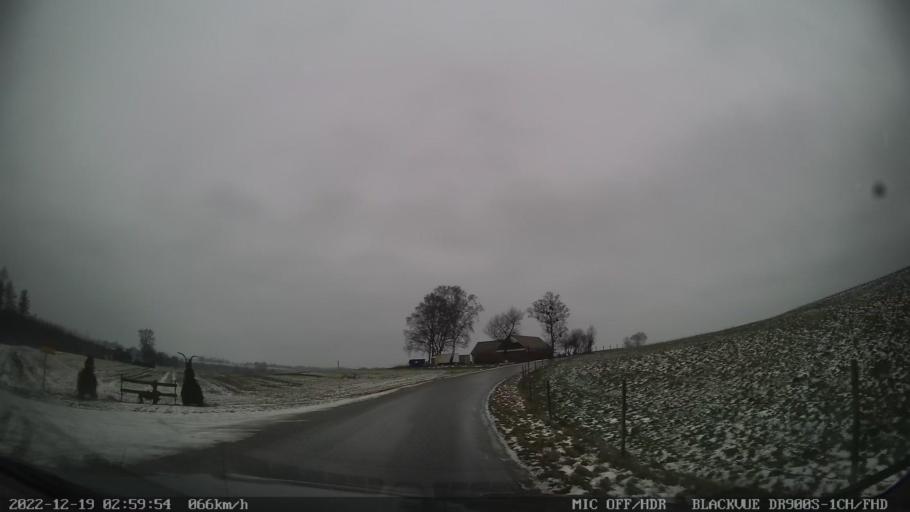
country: SE
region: Skane
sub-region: Tomelilla Kommun
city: Tomelilla
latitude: 55.5145
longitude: 14.0313
